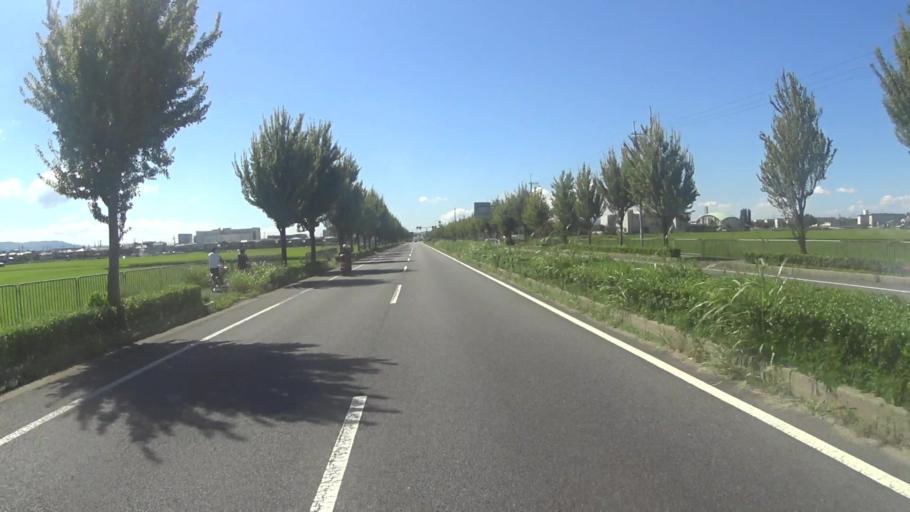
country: JP
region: Kyoto
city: Uji
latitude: 34.8855
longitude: 135.7632
